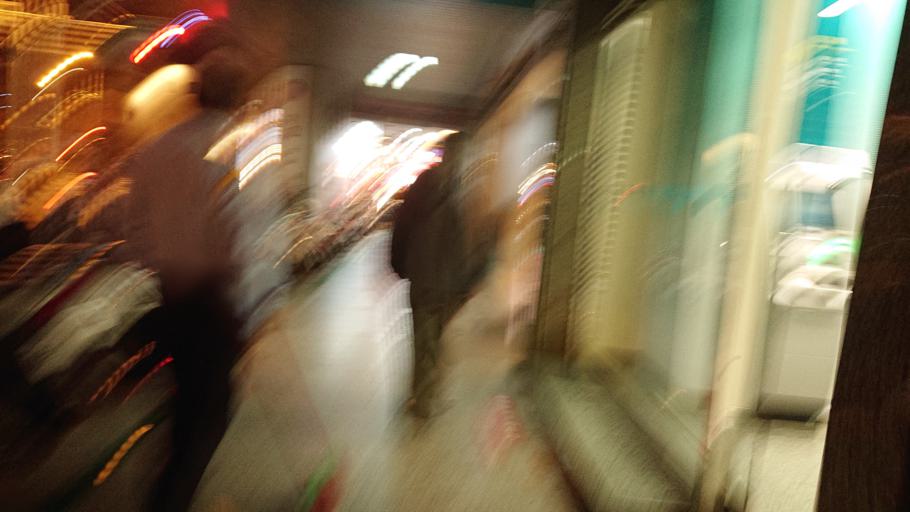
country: TW
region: Taiwan
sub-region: Tainan
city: Tainan
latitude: 22.9952
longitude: 120.1972
